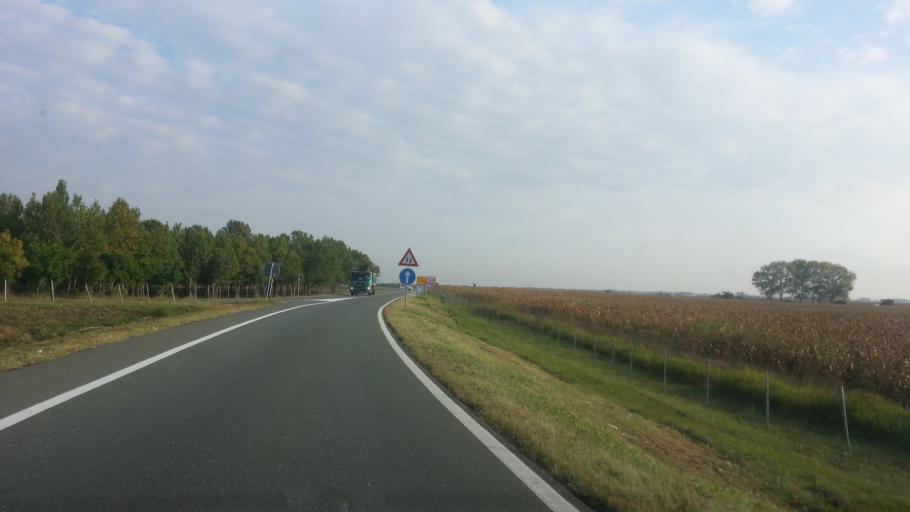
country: RS
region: Autonomna Pokrajina Vojvodina
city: Nova Pazova
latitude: 44.9839
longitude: 20.2190
